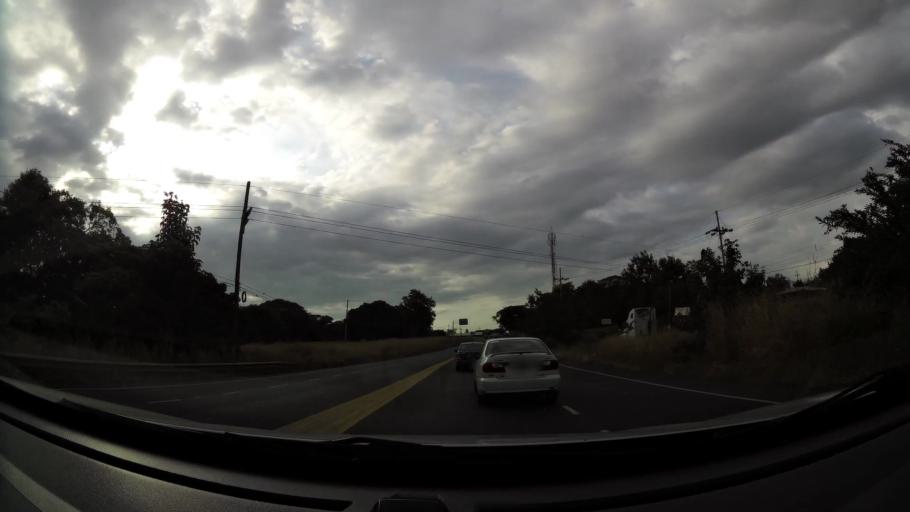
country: CR
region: Puntarenas
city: Esparza
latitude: 9.8927
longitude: -84.6490
